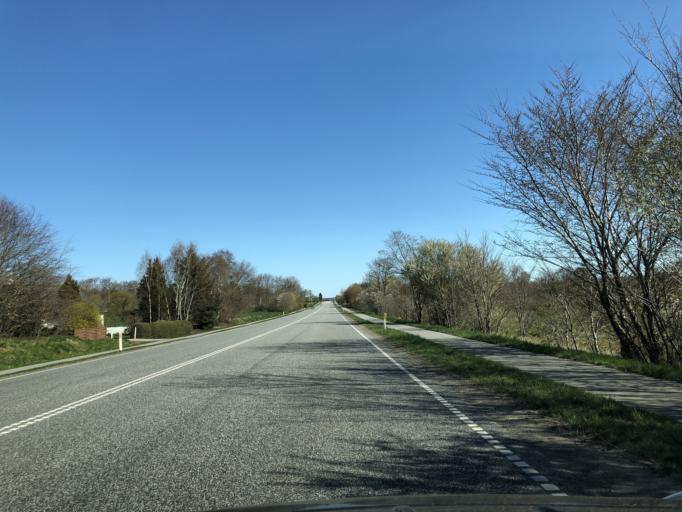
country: DK
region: North Denmark
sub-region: Rebild Kommune
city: Stovring
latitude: 56.9101
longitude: 9.8491
